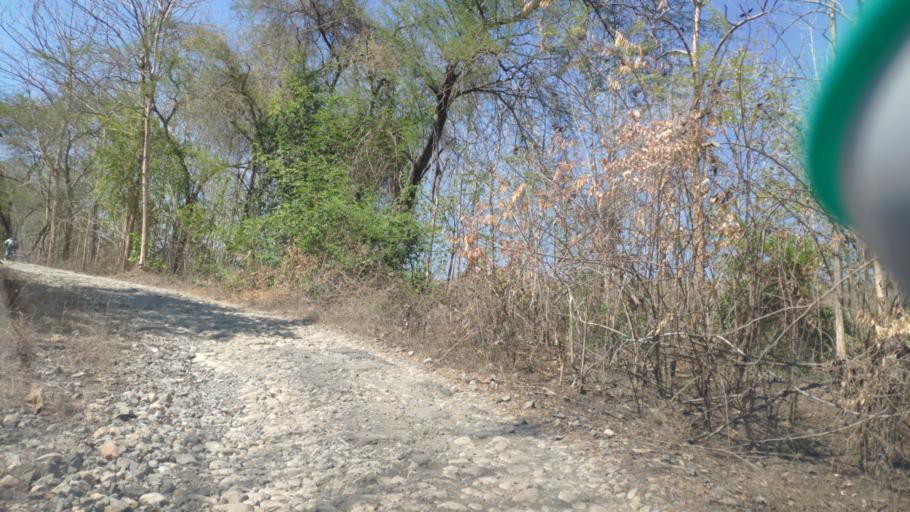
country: ID
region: East Java
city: Krajan Jamprong
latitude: -7.0033
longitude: 111.6060
